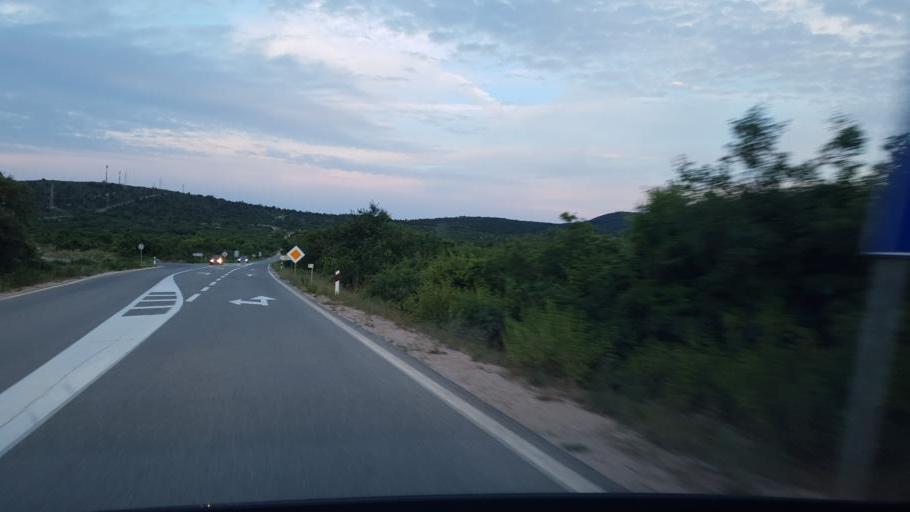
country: HR
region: Primorsko-Goranska
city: Punat
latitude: 45.0349
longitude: 14.6576
